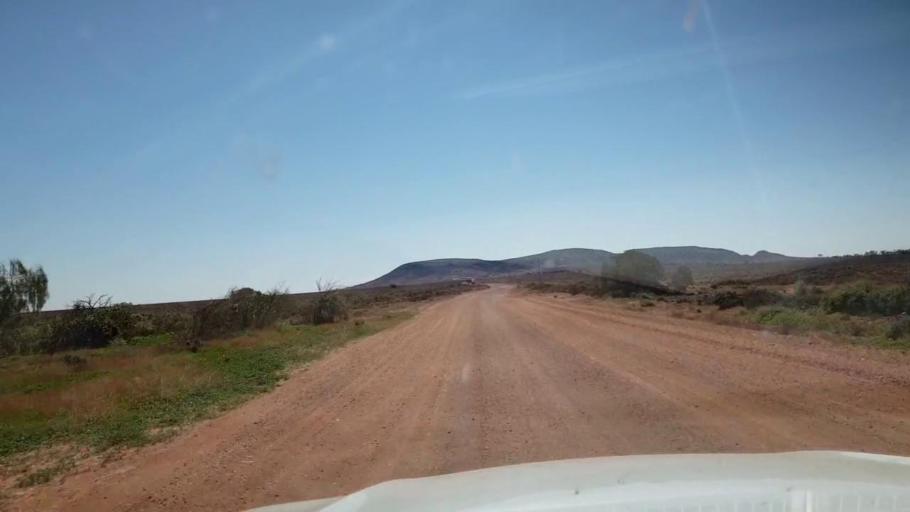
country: AU
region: South Australia
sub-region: Whyalla
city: Whyalla
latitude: -32.7148
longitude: 137.1427
